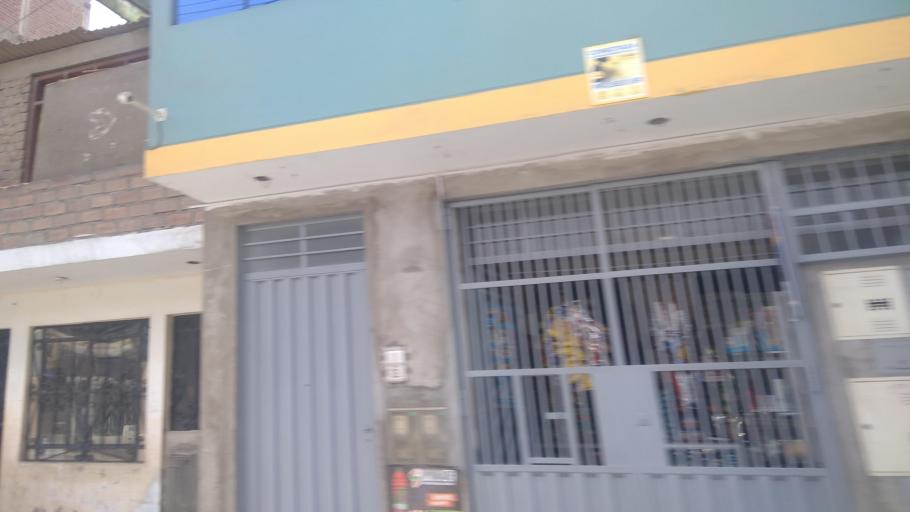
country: PE
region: Lima
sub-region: Lima
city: Independencia
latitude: -11.9687
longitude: -76.9880
